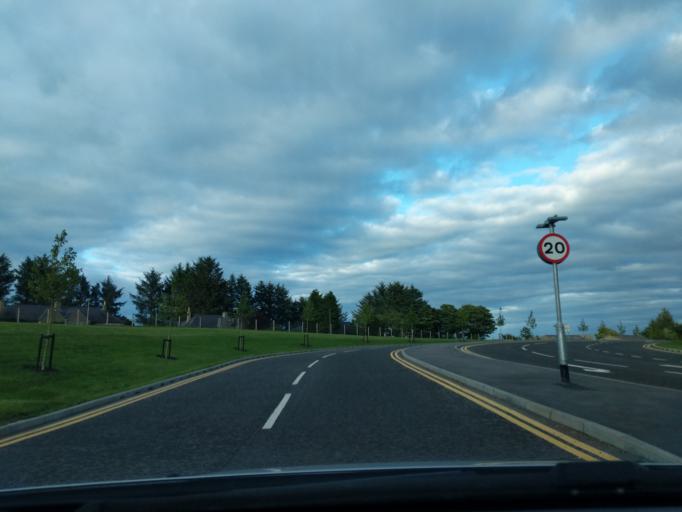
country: GB
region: Scotland
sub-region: Aberdeen City
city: Dyce
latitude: 57.1895
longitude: -2.1996
